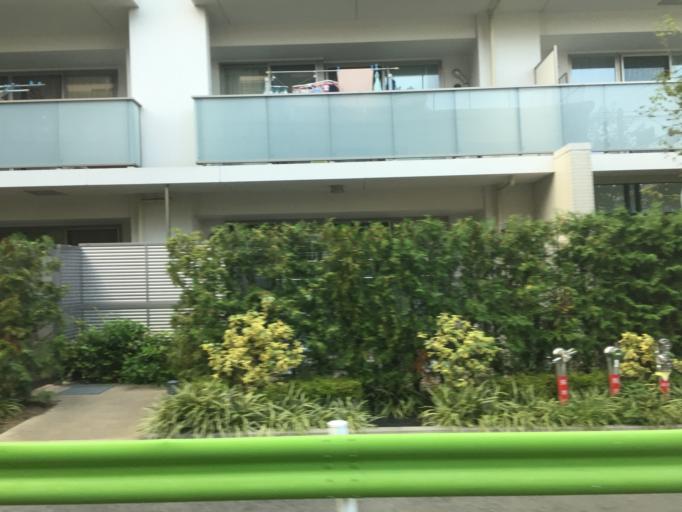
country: JP
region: Kanagawa
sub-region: Kawasaki-shi
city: Kawasaki
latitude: 35.5652
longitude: 139.6852
